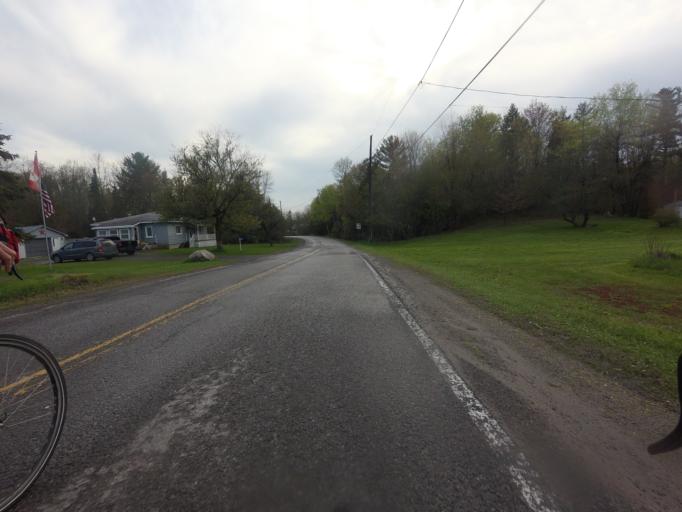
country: CA
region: Ontario
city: Carleton Place
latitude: 45.1908
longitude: -76.3302
